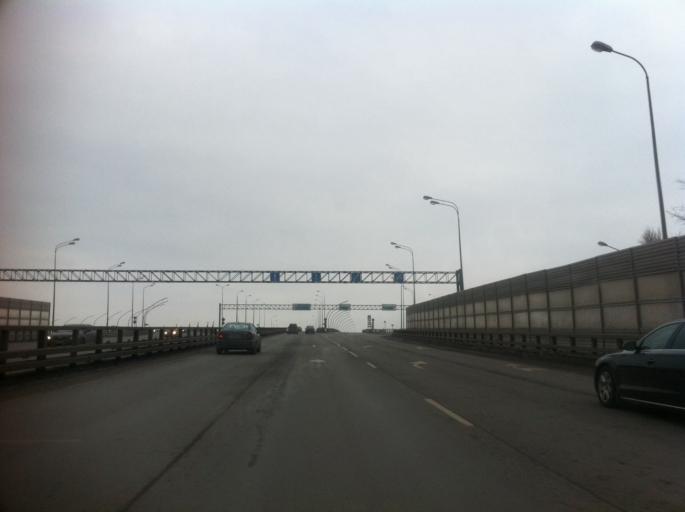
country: RU
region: St.-Petersburg
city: Dachnoye
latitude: 59.8369
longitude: 30.2643
